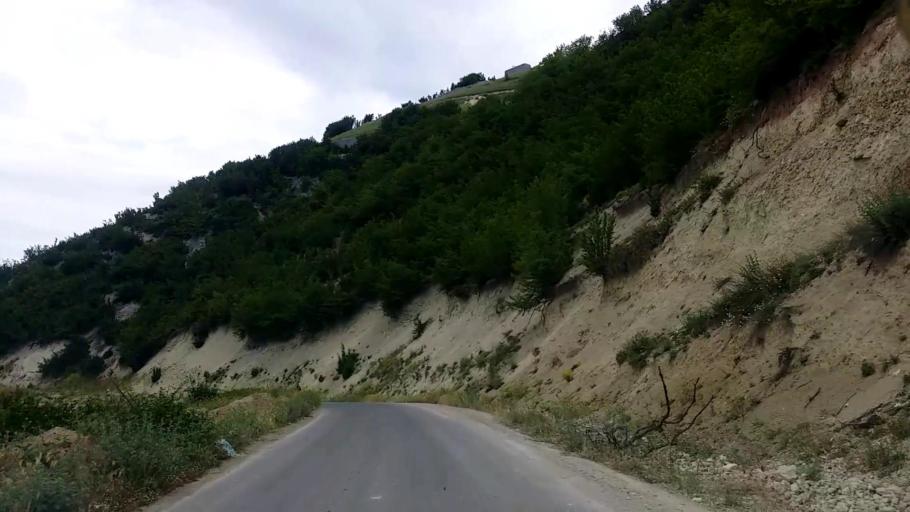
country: IR
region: Mazandaran
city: Chalus
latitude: 36.5418
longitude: 51.2724
